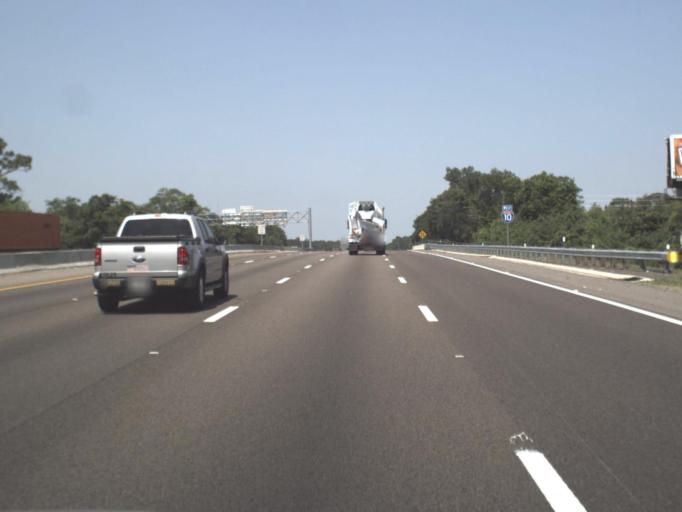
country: US
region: Florida
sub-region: Duval County
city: Jacksonville
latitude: 30.3152
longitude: -81.7818
